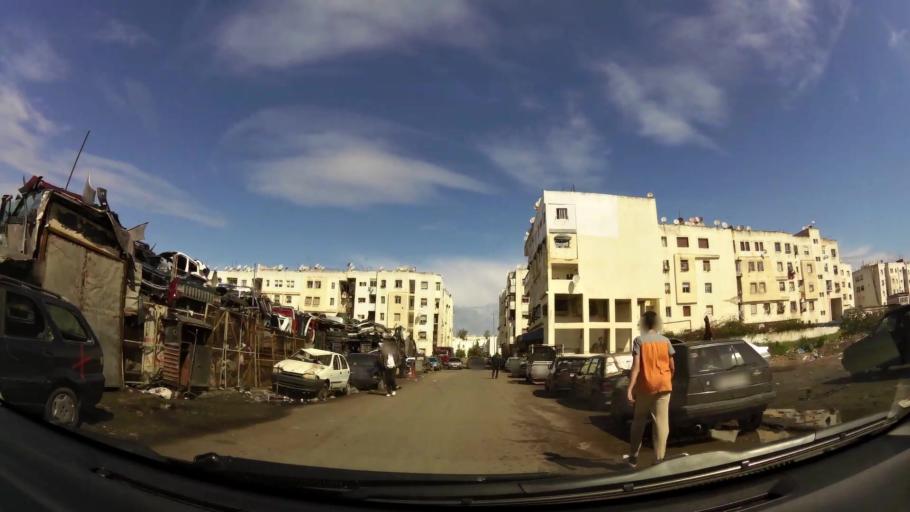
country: MA
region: Grand Casablanca
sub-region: Casablanca
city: Casablanca
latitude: 33.5653
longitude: -7.6801
